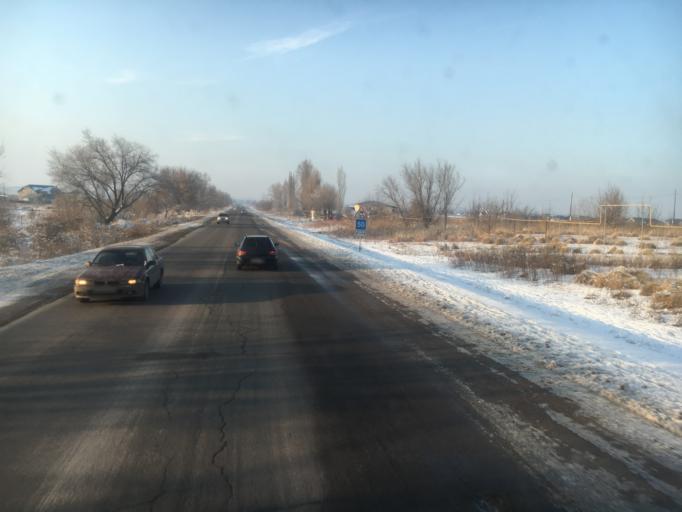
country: KZ
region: Almaty Oblysy
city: Burunday
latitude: 43.3416
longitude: 76.6580
